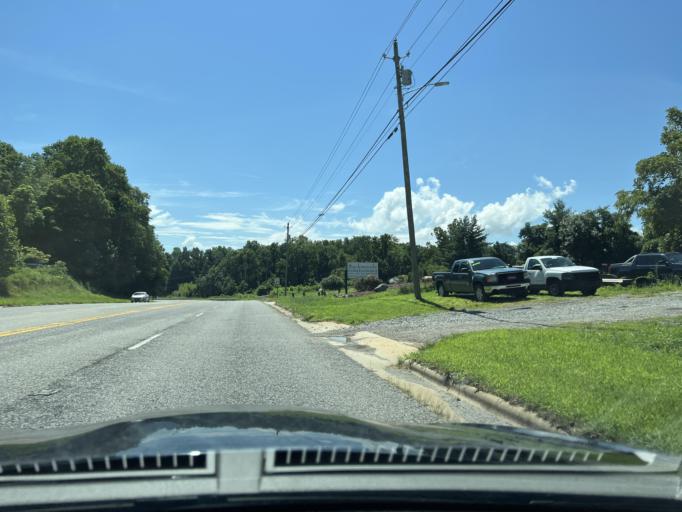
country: US
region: North Carolina
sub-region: Buncombe County
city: Fairview
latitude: 35.5238
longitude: -82.4216
